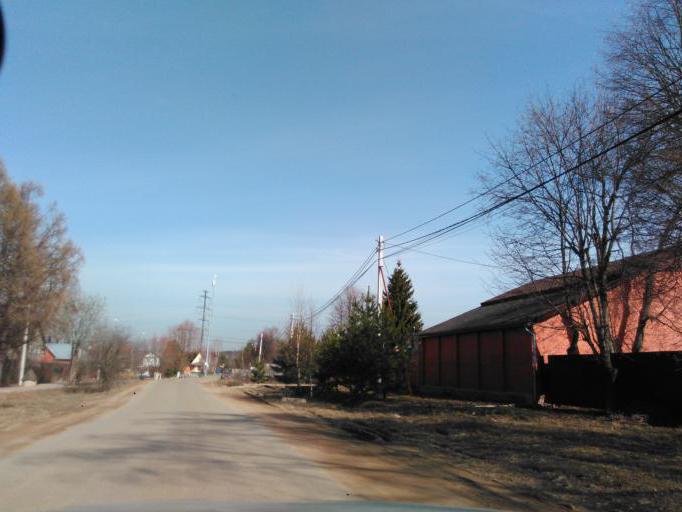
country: RU
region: Moskovskaya
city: Opalikha
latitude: 55.8803
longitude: 37.2649
